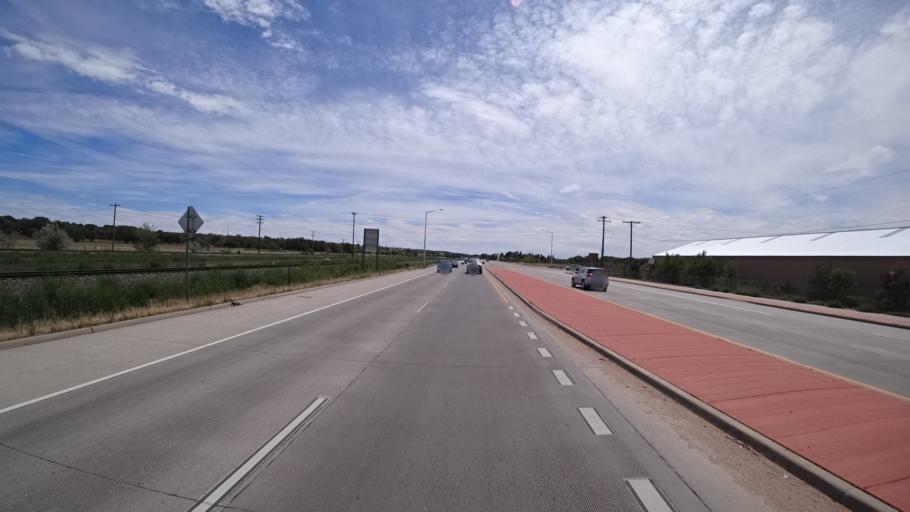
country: US
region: Colorado
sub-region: El Paso County
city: Security-Widefield
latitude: 38.7199
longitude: -104.7168
